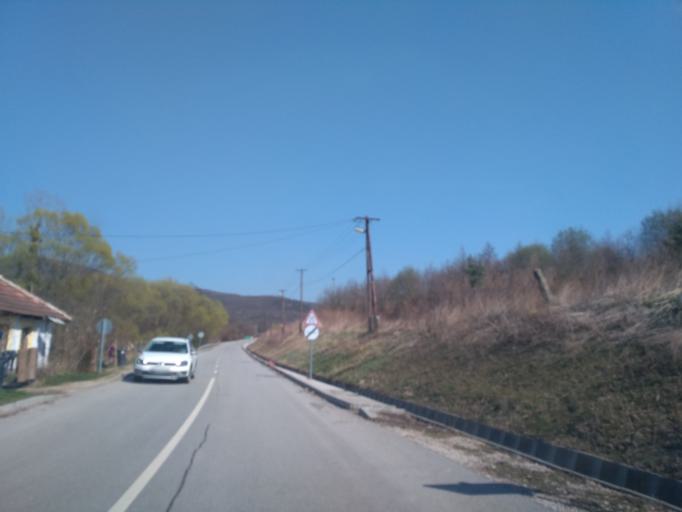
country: HU
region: Borsod-Abauj-Zemplen
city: Gonc
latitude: 48.5451
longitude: 21.3396
